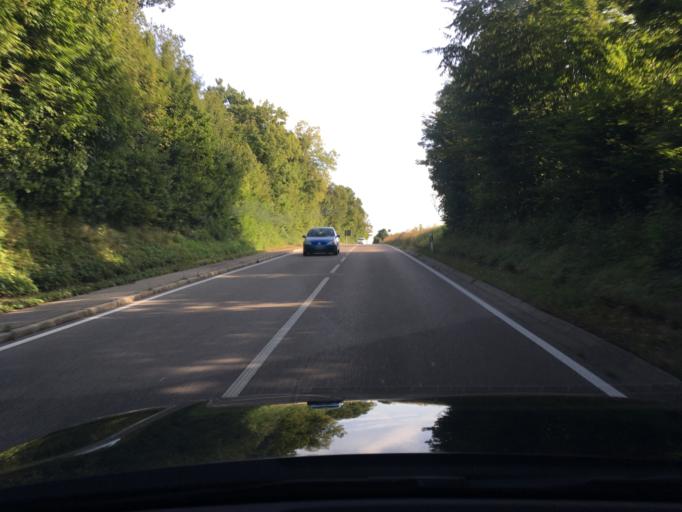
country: DE
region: Baden-Wuerttemberg
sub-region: Regierungsbezirk Stuttgart
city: Schorndorf
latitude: 48.7818
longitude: 9.5554
